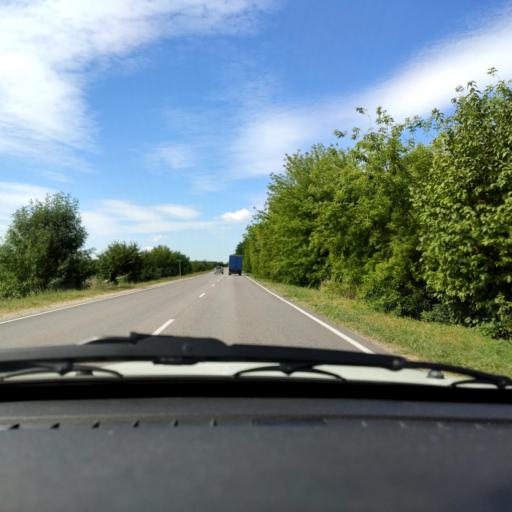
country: RU
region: Voronezj
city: Volya
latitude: 51.7034
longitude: 39.5187
